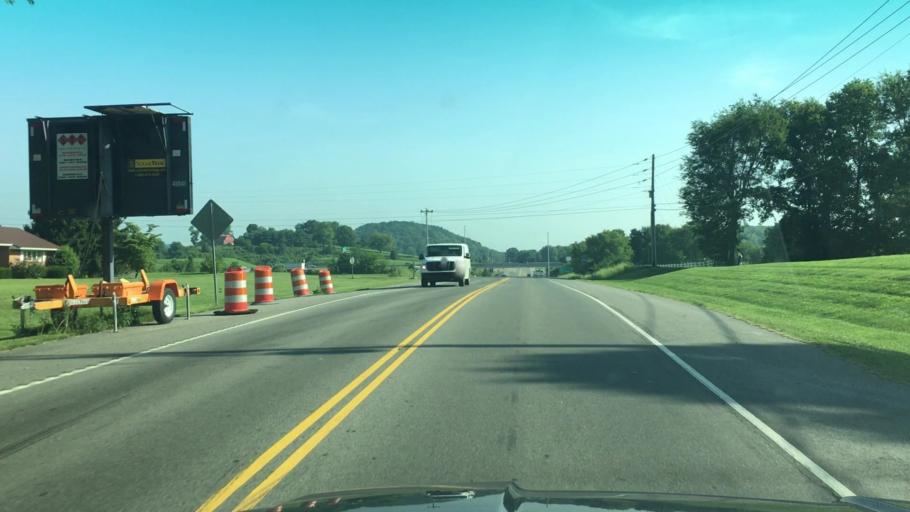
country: US
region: Tennessee
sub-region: Williamson County
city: Thompson's Station
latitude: 35.8172
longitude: -86.8515
